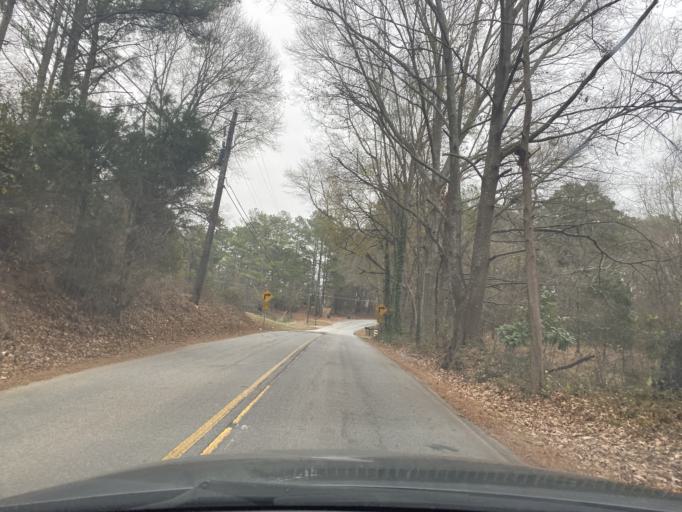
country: US
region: Georgia
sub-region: DeKalb County
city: Pine Mountain
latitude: 33.6907
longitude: -84.1593
